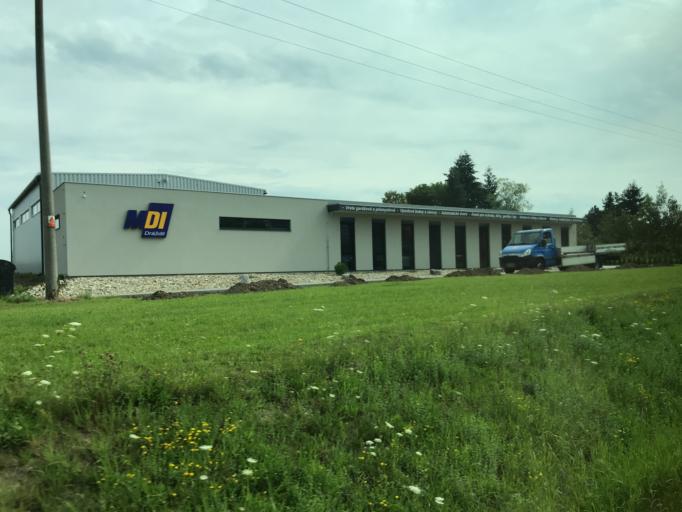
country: CZ
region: Jihocesky
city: Kamenny Ujezd
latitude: 48.8983
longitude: 14.4421
